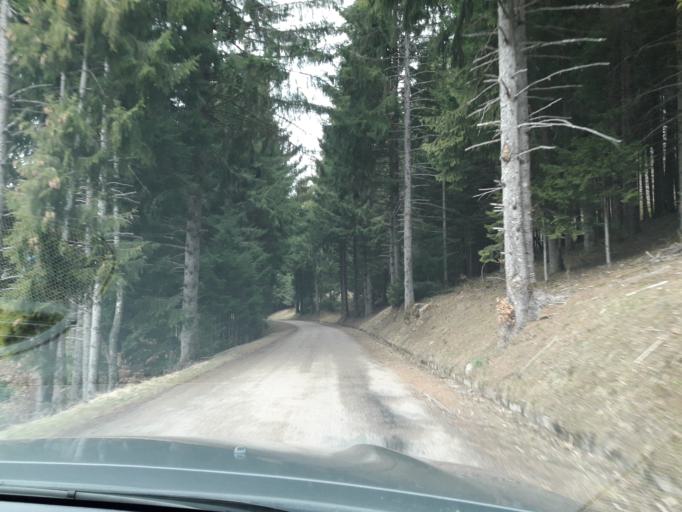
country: FR
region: Rhone-Alpes
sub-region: Departement de l'Isere
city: Le Champ-pres-Froges
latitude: 45.2439
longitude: 5.9795
